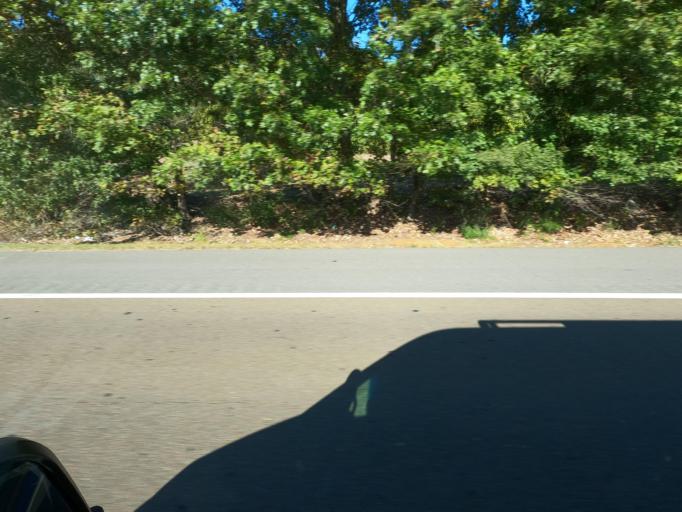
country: US
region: Tennessee
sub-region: Tipton County
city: Munford
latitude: 35.4307
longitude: -89.8075
